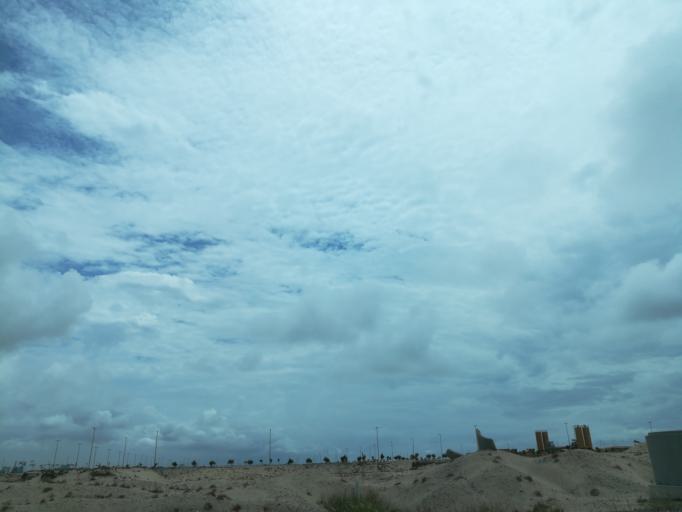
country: NG
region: Lagos
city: Lagos
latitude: 6.4054
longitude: 3.4098
